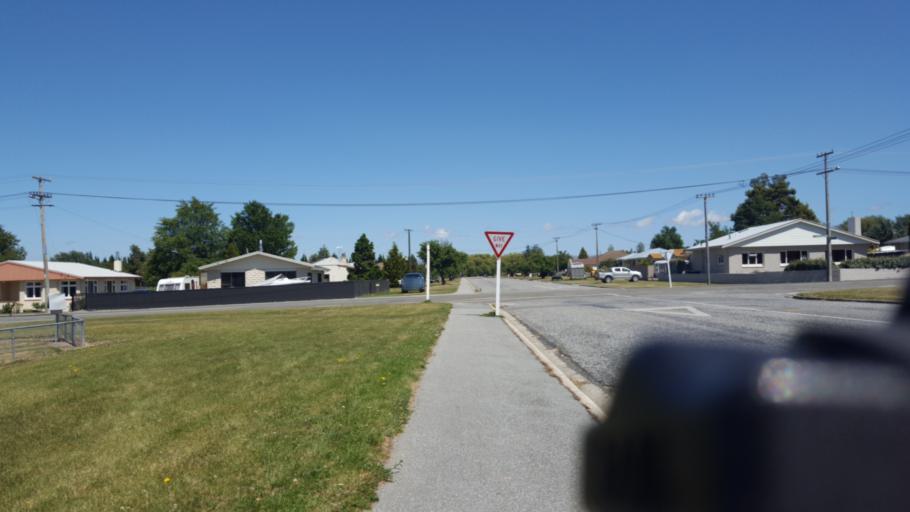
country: NZ
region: Otago
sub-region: Dunedin City
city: Dunedin
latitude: -45.1269
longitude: 170.1010
